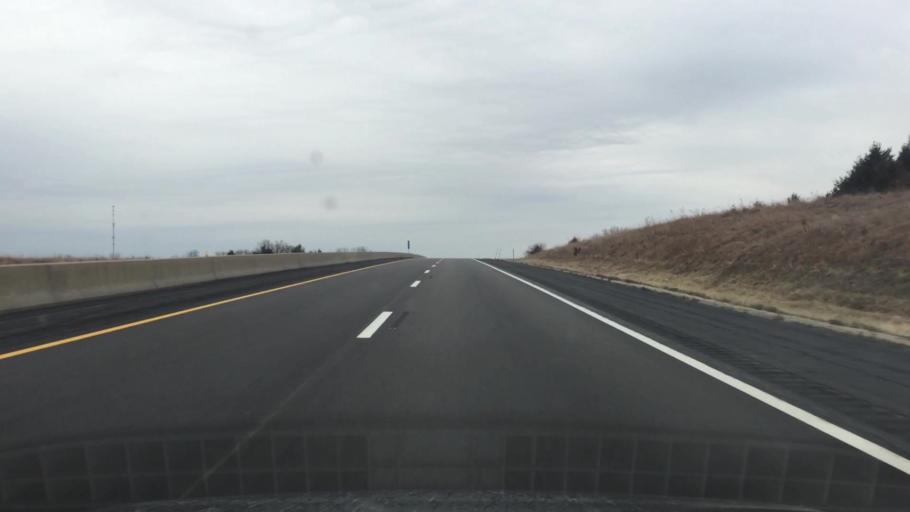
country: US
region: Kansas
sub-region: Shawnee County
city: Auburn
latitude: 38.8087
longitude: -95.8999
